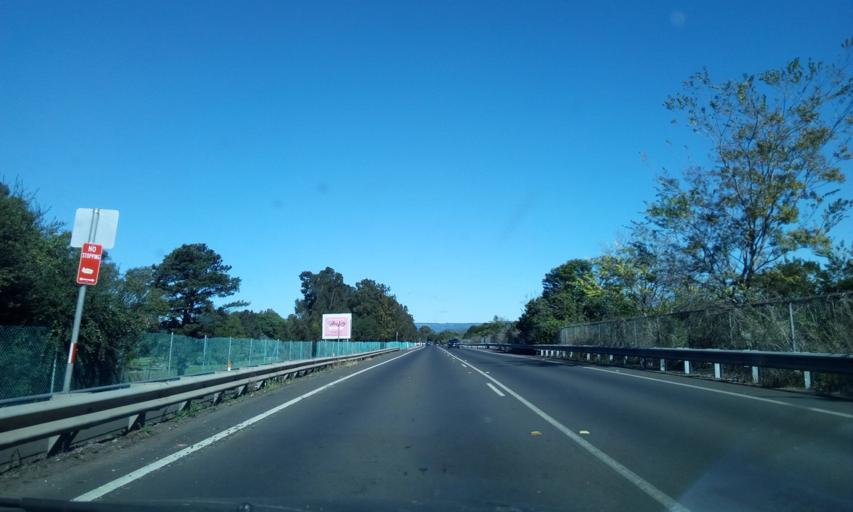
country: AU
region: New South Wales
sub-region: Wollongong
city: Koonawarra
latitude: -34.4763
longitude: 150.8089
